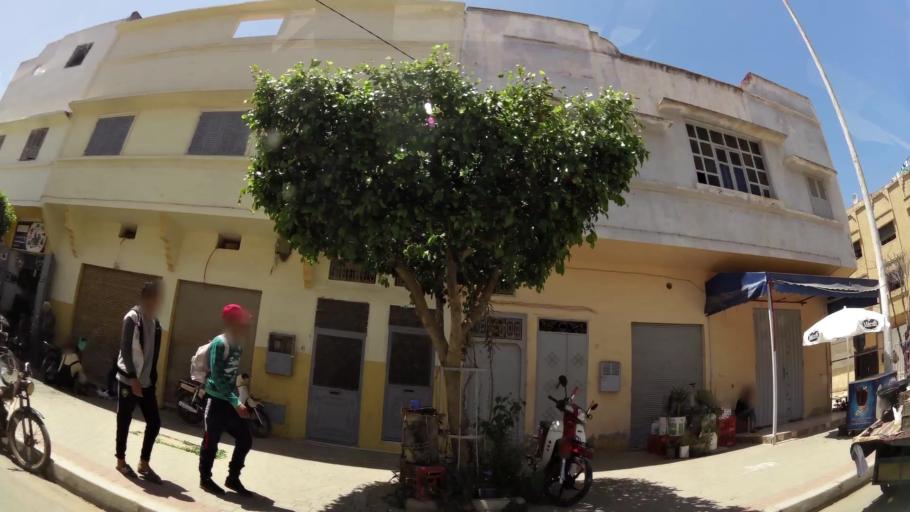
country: MA
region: Rabat-Sale-Zemmour-Zaer
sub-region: Khemisset
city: Khemisset
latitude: 33.8313
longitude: -6.0743
